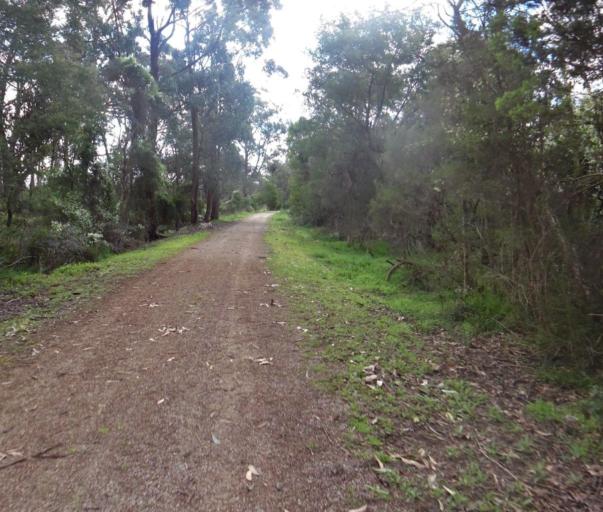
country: AU
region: Victoria
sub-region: Bass Coast
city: North Wonthaggi
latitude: -38.6640
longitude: 146.0242
